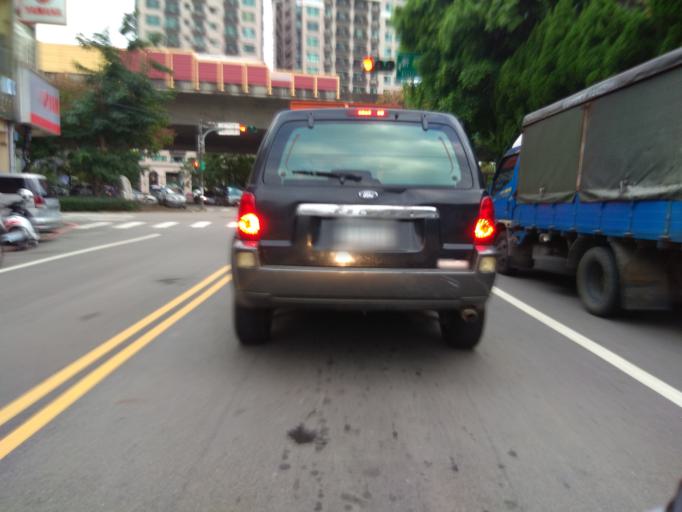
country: TW
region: Taiwan
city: Daxi
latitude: 24.8606
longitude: 121.2157
